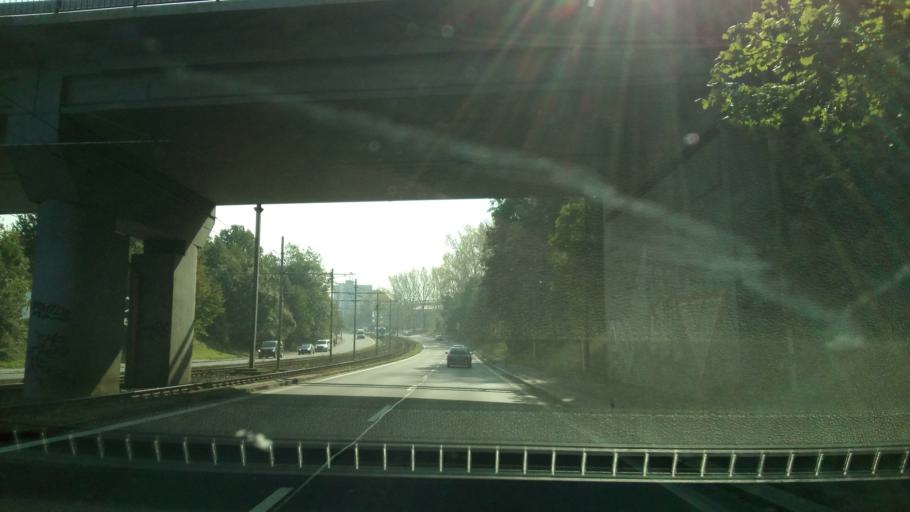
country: CZ
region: Moravskoslezsky
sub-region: Okres Ostrava-Mesto
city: Ostrava
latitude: 49.8186
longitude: 18.2367
